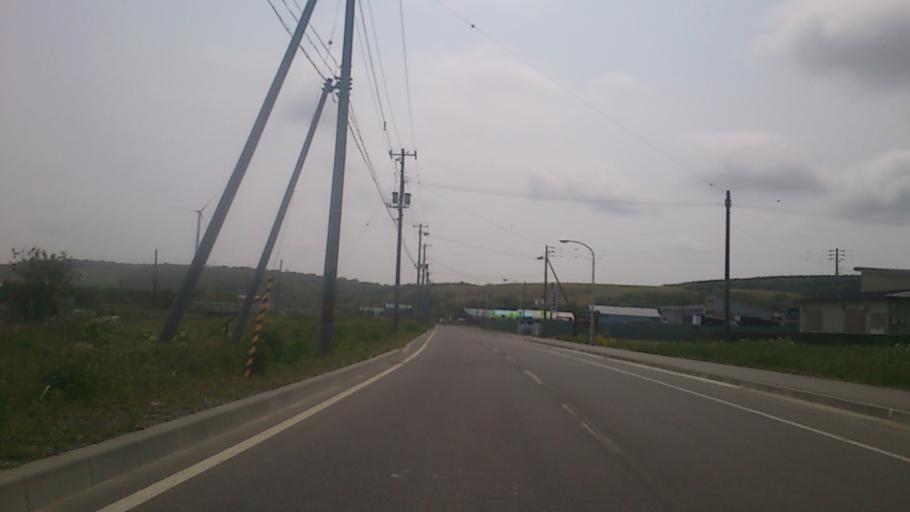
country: JP
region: Hokkaido
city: Nemuro
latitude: 43.2847
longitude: 145.5687
